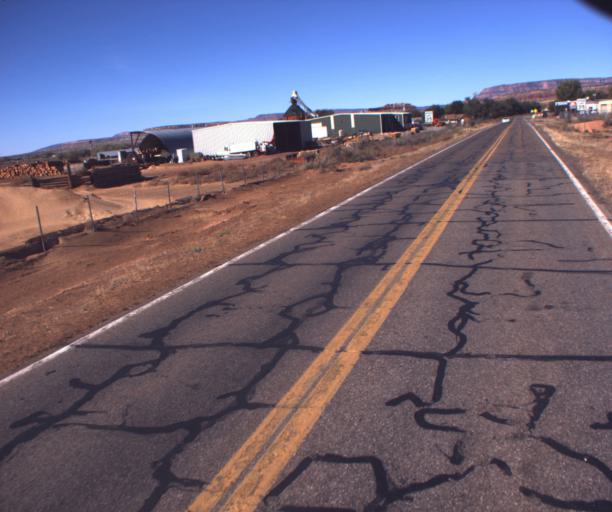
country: US
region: Arizona
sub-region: Coconino County
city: Fredonia
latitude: 36.9388
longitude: -112.5187
